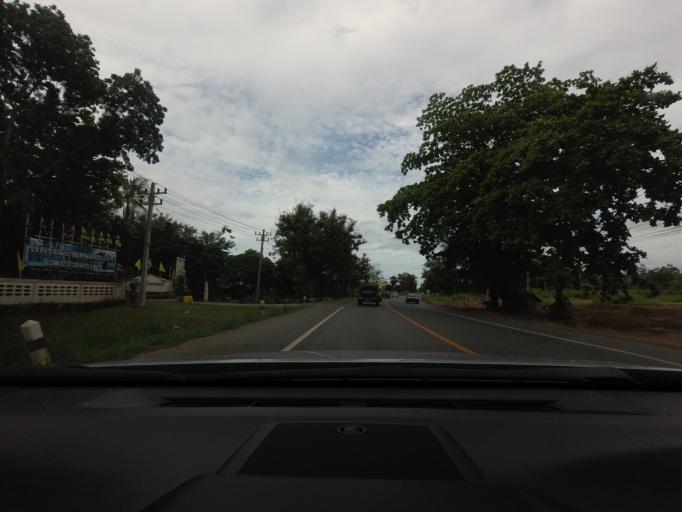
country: TH
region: Prachuap Khiri Khan
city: Hua Hin
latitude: 12.5819
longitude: 99.8488
